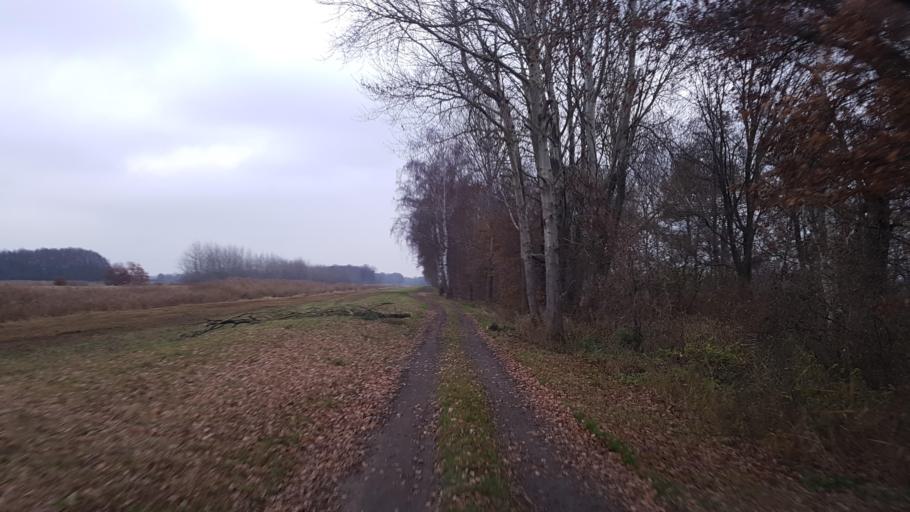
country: DE
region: Brandenburg
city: Schraden
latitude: 51.4599
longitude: 13.6973
